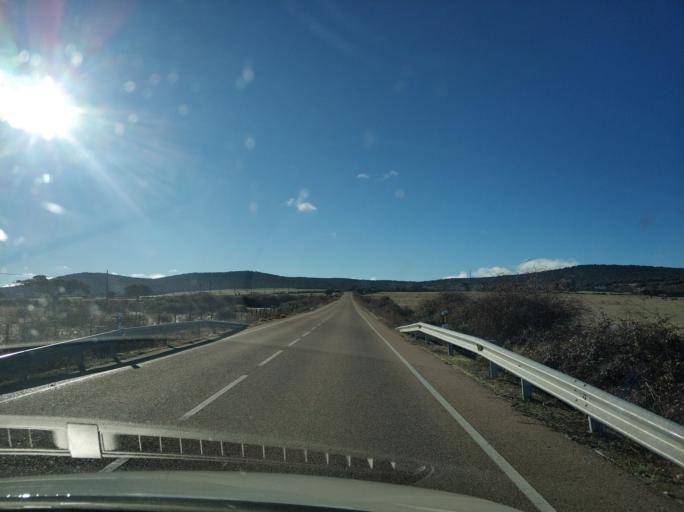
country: ES
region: Castille and Leon
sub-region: Provincia de Salamanca
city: Vecinos
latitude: 40.7385
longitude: -5.8814
